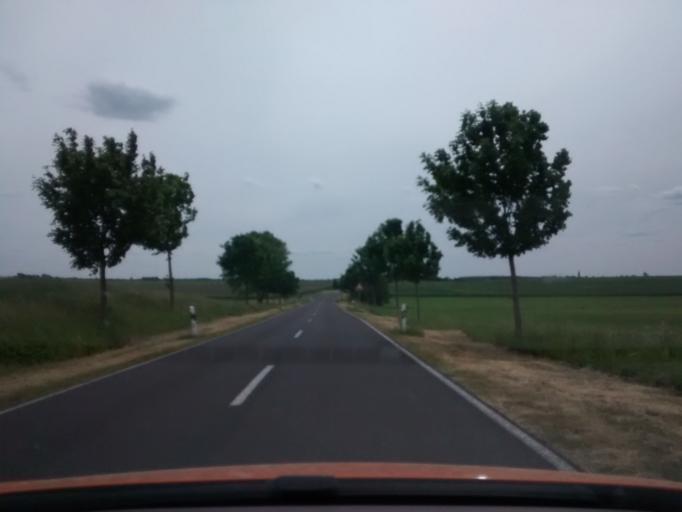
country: DE
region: Brandenburg
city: Juterbog
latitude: 51.9660
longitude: 13.0778
